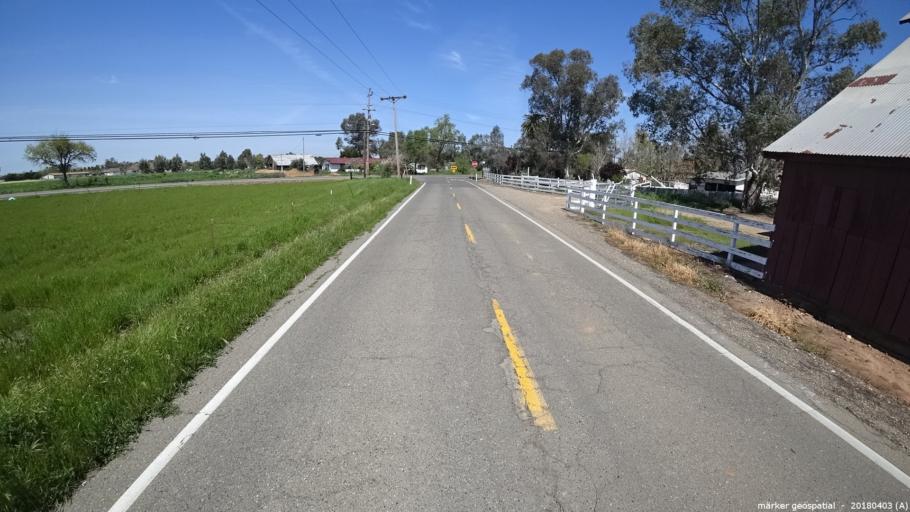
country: US
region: California
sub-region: Sacramento County
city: Wilton
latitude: 38.3986
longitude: -121.2607
